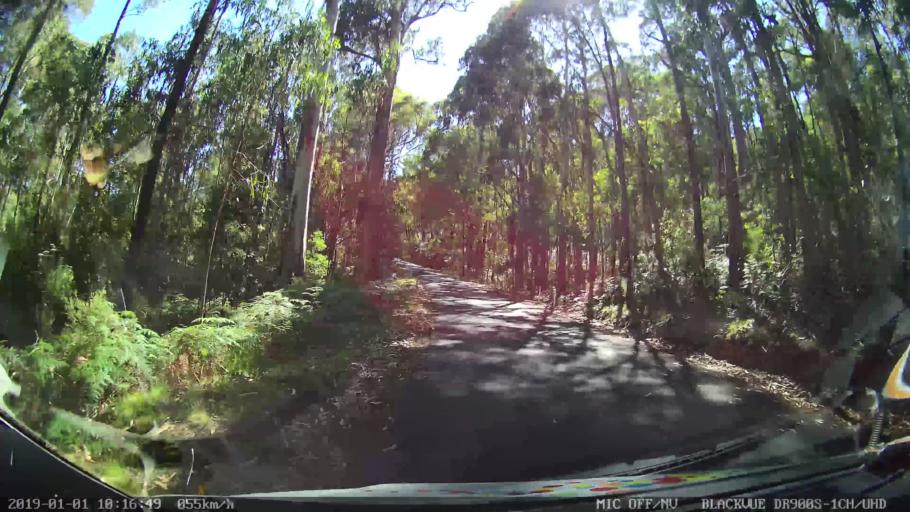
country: AU
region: New South Wales
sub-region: Snowy River
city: Jindabyne
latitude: -36.0929
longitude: 148.1708
